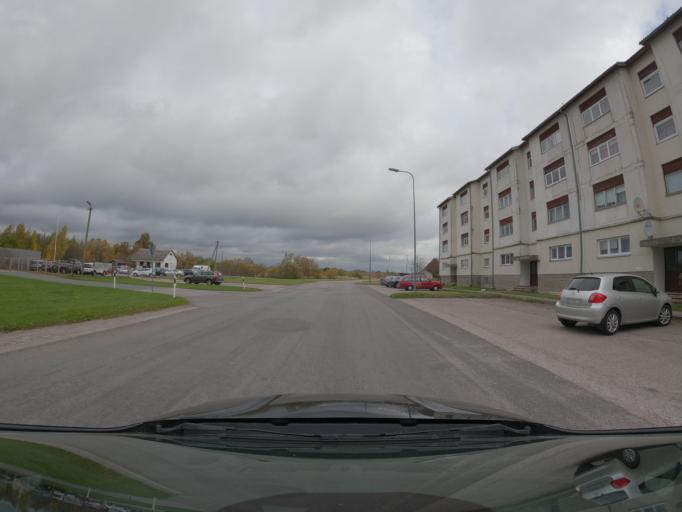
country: EE
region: Saare
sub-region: Kuressaare linn
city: Kuressaare
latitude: 58.2633
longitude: 22.4817
